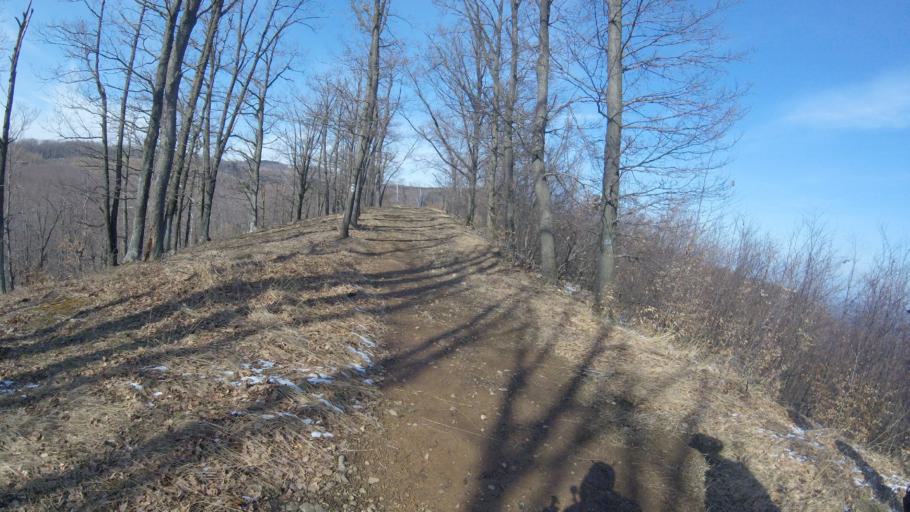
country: HU
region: Heves
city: Paradsasvar
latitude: 47.9060
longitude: 19.9522
